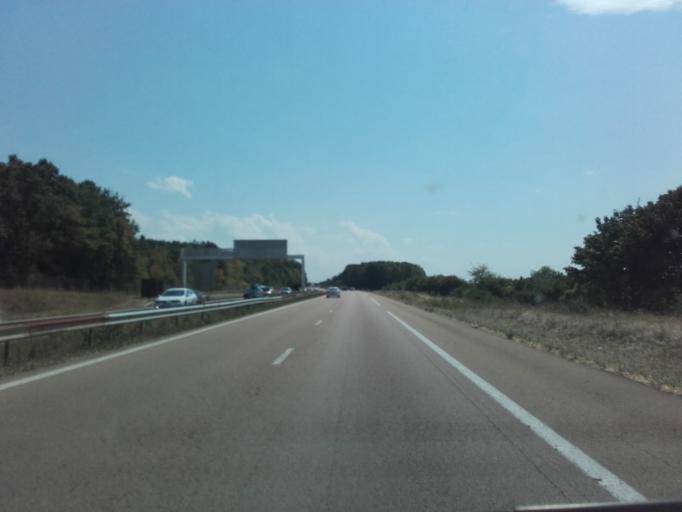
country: FR
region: Bourgogne
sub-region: Departement de l'Yonne
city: Joux-la-Ville
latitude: 47.6376
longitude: 3.9067
